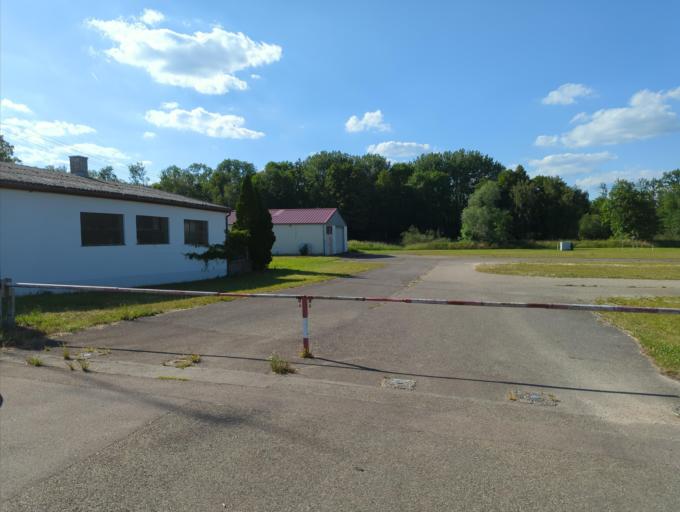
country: DE
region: Bavaria
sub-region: Swabia
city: Guenzburg
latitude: 48.4617
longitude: 10.2766
